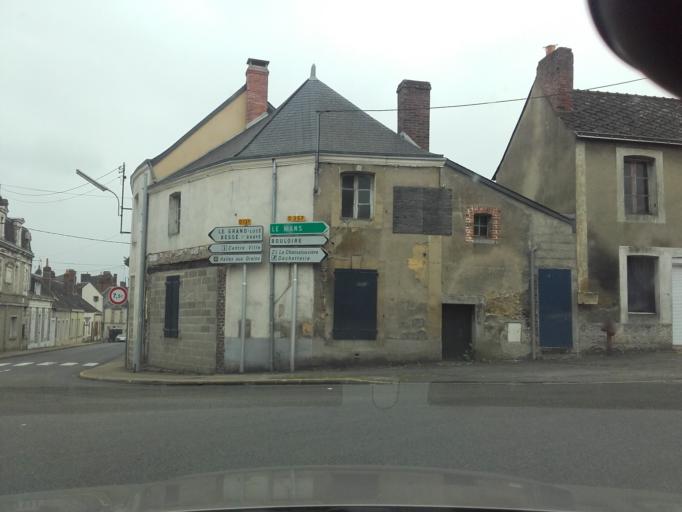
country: FR
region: Pays de la Loire
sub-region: Departement de la Sarthe
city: Saint-Calais
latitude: 47.9234
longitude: 0.7428
